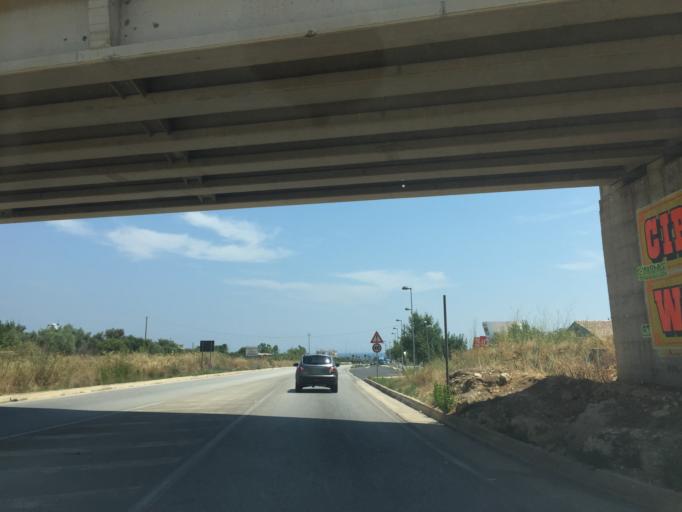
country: IT
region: Sicily
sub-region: Provincia di Siracusa
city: Avola
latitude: 36.9209
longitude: 15.1427
